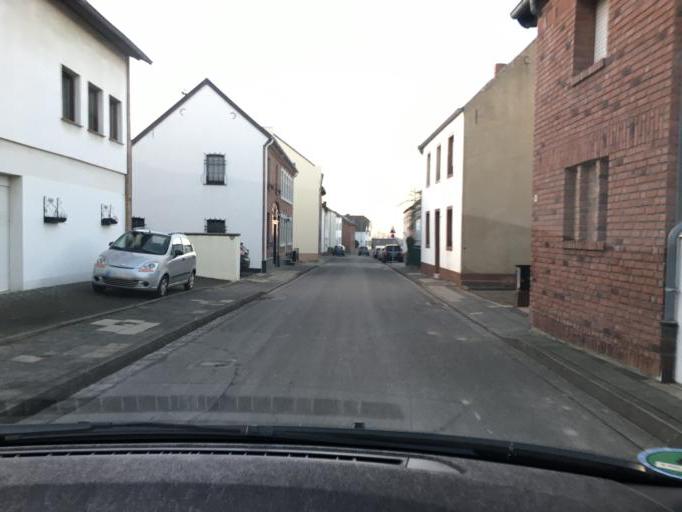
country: DE
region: North Rhine-Westphalia
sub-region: Regierungsbezirk Koln
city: Kreuzau
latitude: 50.7688
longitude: 6.4475
